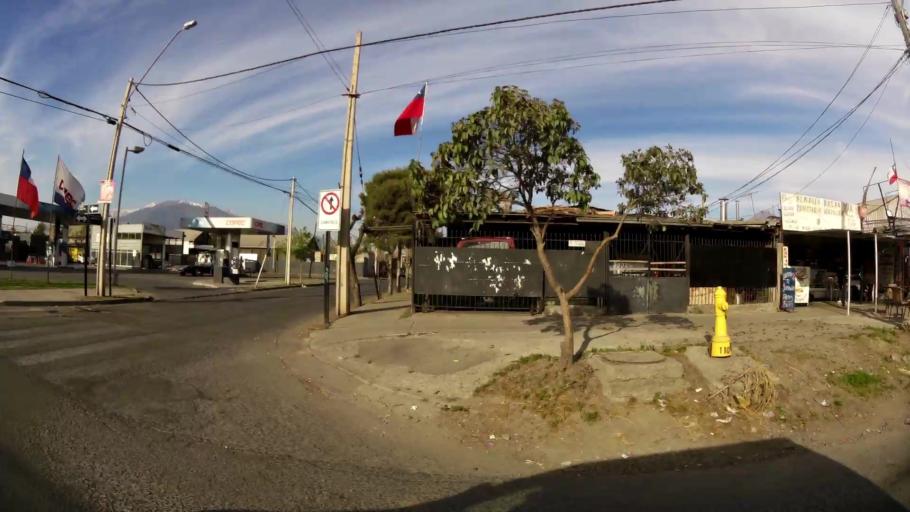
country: CL
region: Santiago Metropolitan
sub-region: Provincia de Cordillera
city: Puente Alto
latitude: -33.6171
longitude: -70.5743
